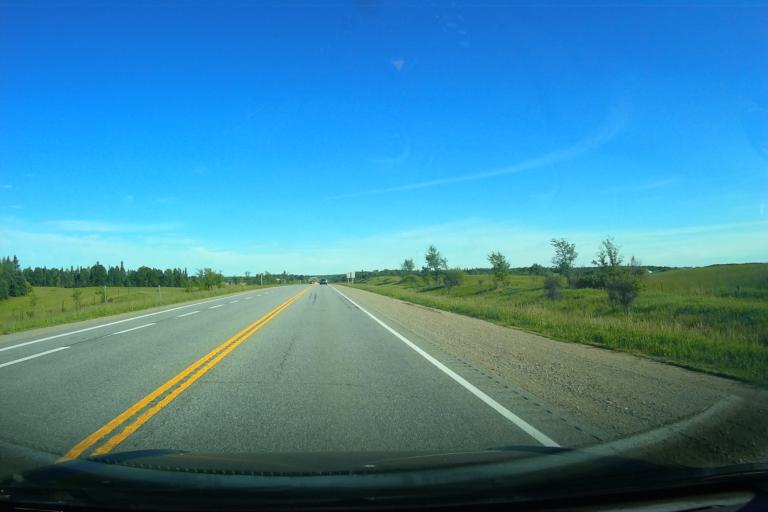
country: CA
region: Ontario
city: Renfrew
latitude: 45.5123
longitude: -76.6795
